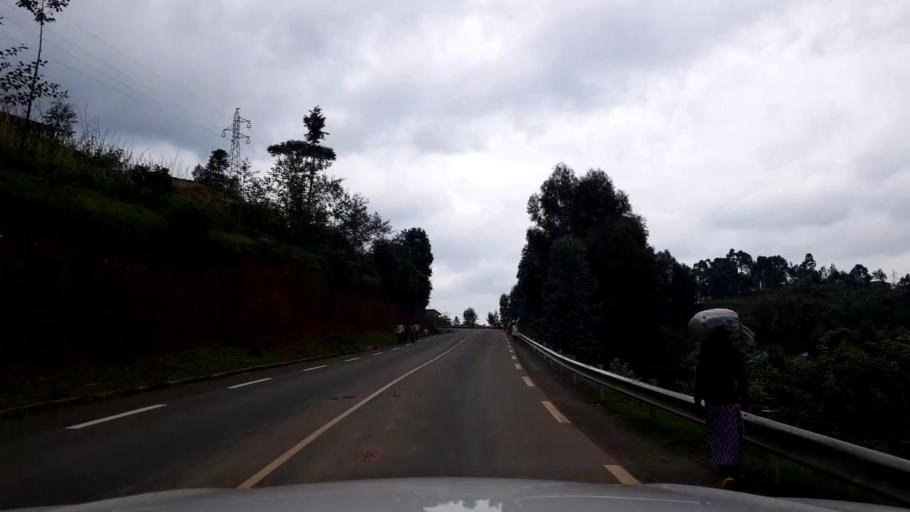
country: RW
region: Western Province
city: Kibuye
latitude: -1.8814
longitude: 29.3507
